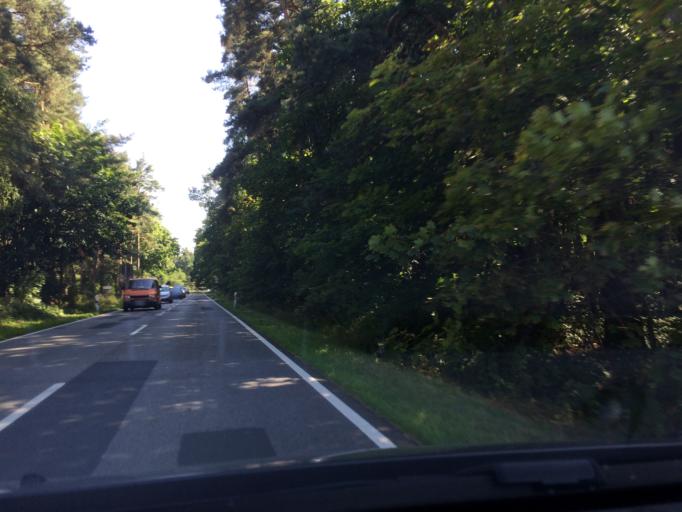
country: DE
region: Mecklenburg-Vorpommern
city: Barth
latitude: 54.3674
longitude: 12.6731
